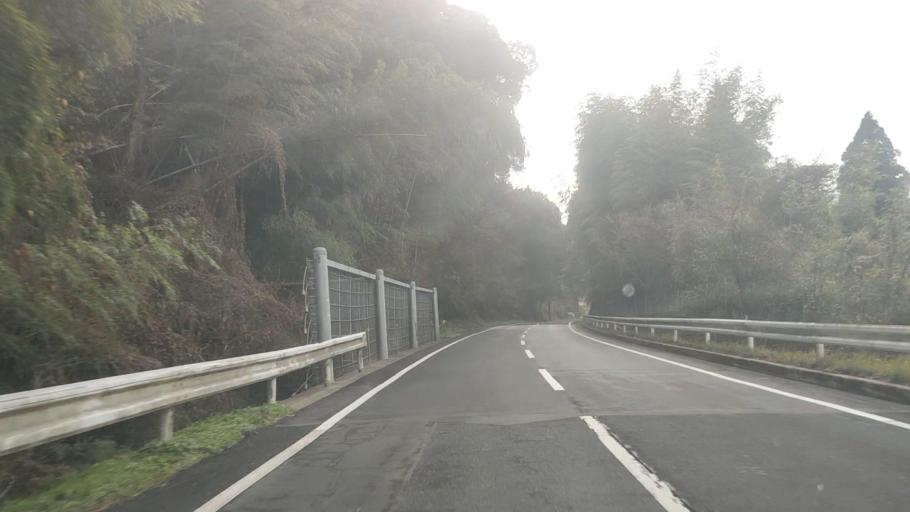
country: JP
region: Kagoshima
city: Okuchi-shinohara
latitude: 31.9679
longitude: 130.7399
